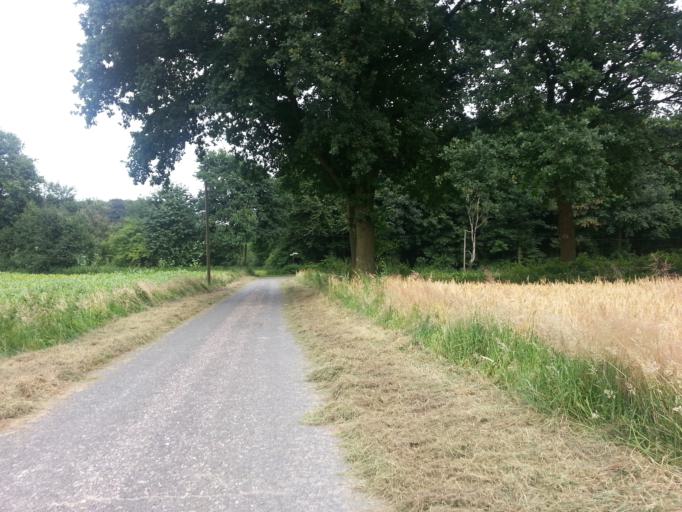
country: DE
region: North Rhine-Westphalia
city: Oer-Erkenschwick
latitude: 51.6558
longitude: 7.2637
